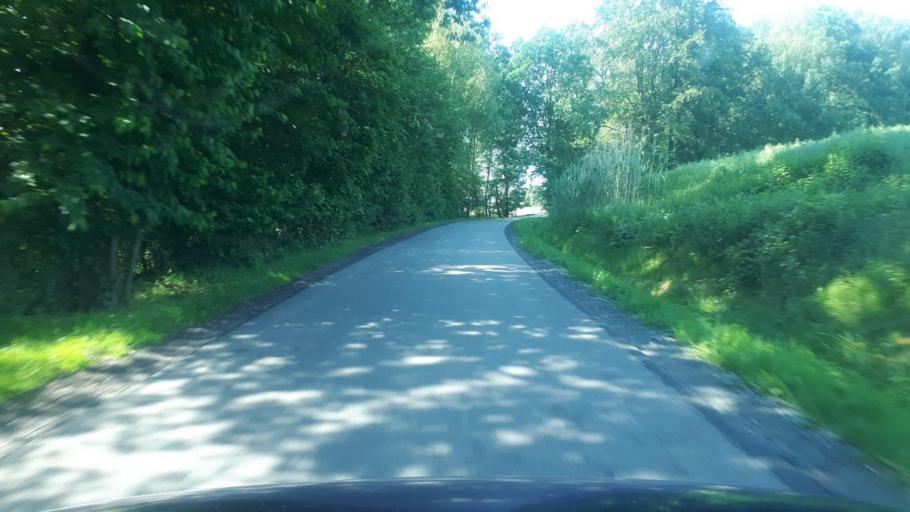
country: PL
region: Silesian Voivodeship
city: Janowice
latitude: 49.8977
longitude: 19.1089
